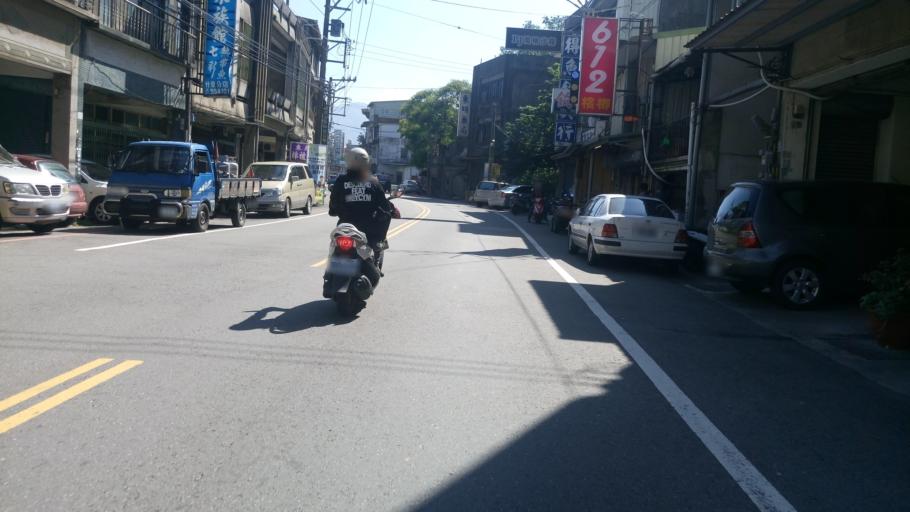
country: TW
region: Taiwan
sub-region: Hsinchu
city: Zhubei
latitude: 24.7310
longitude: 121.0903
